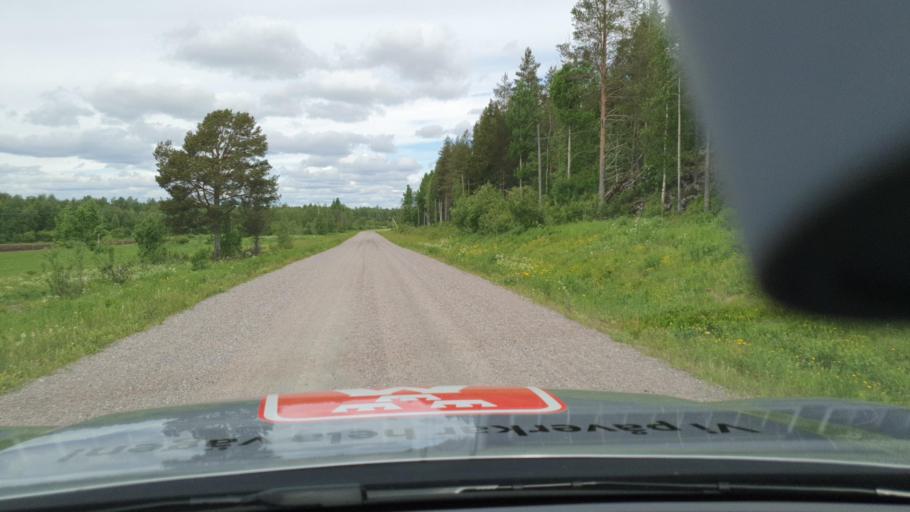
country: FI
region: Lapland
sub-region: Torniolaakso
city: Ylitornio
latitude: 65.9648
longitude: 23.7959
